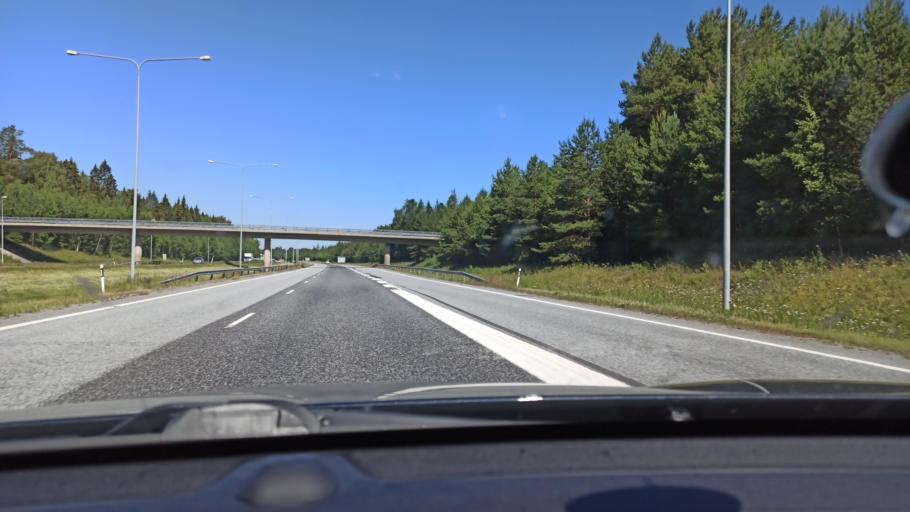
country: FI
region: Ostrobothnia
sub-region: Vaasa
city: Ristinummi
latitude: 63.0570
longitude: 21.7122
